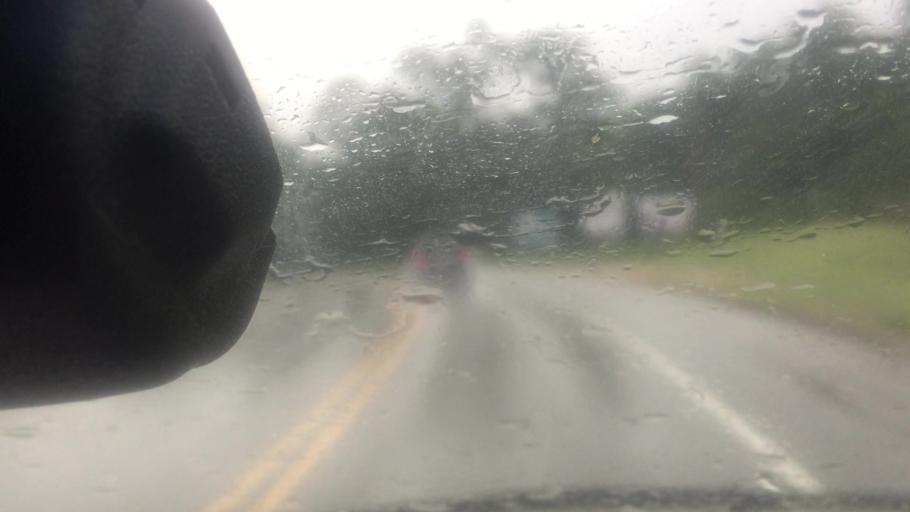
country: US
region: Illinois
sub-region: Madison County
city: Edwardsville
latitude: 38.8271
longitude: -89.9411
